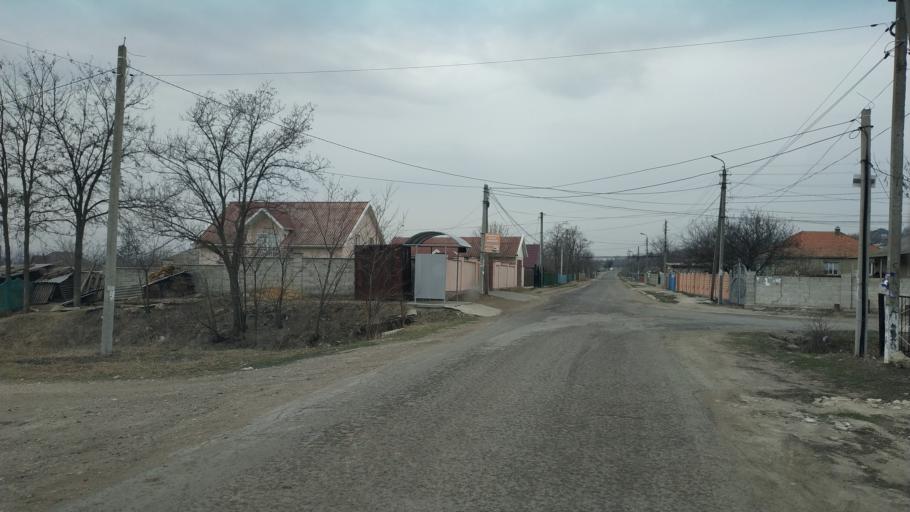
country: MD
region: Chisinau
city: Singera
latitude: 46.9335
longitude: 29.0004
